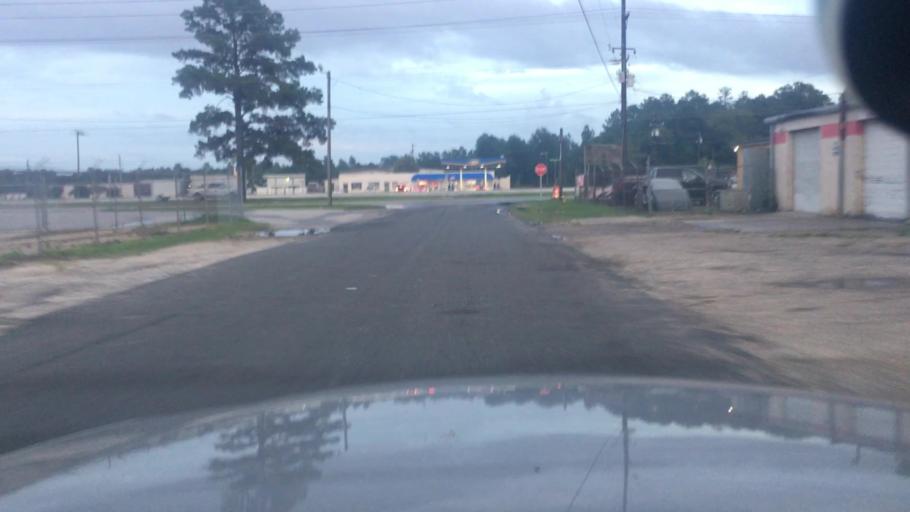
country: US
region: North Carolina
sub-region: Cumberland County
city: Hope Mills
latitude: 34.9827
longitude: -78.9075
